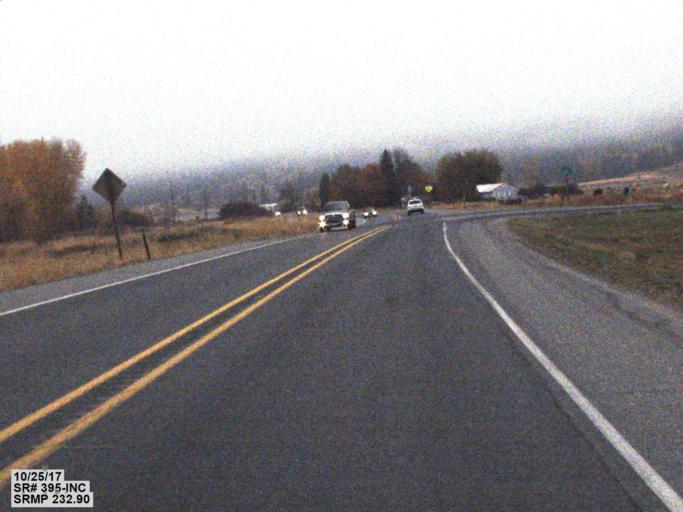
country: US
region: Washington
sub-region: Stevens County
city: Colville
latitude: 48.5787
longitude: -117.9547
